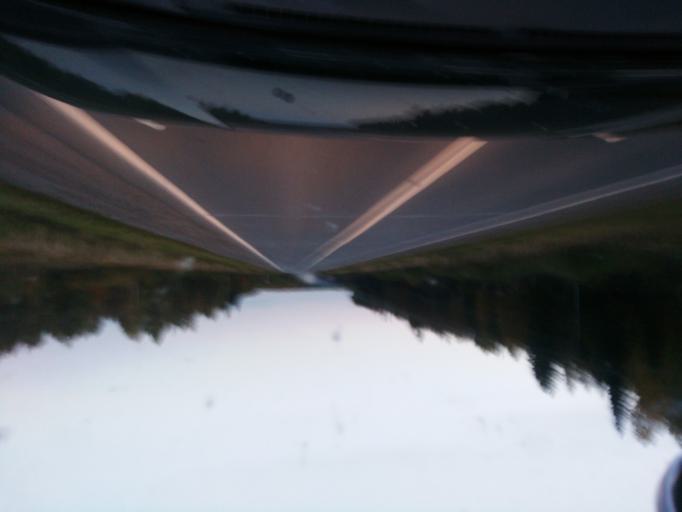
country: RU
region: Perm
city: Verkhnechusovskiye Gorodki
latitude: 58.2319
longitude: 57.2120
